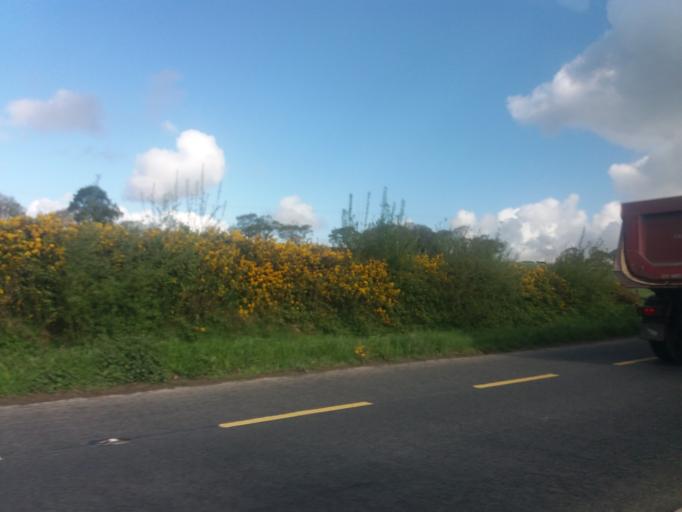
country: IE
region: Leinster
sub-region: Loch Garman
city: Ferns
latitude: 52.5742
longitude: -6.5173
